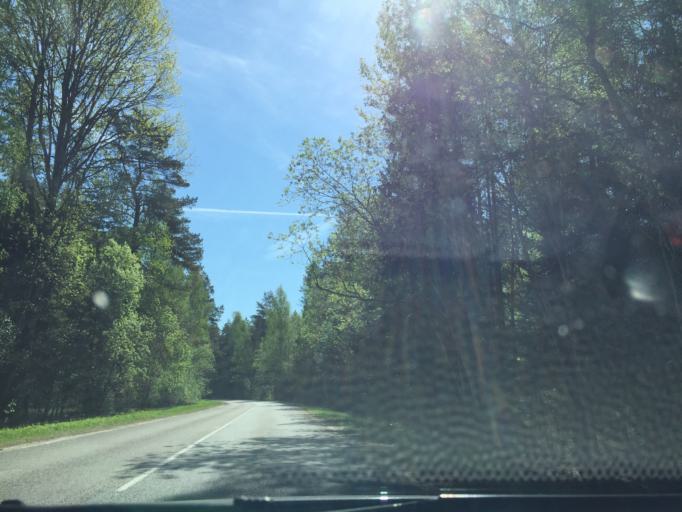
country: LV
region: Garkalne
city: Garkalne
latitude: 57.0070
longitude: 24.4759
